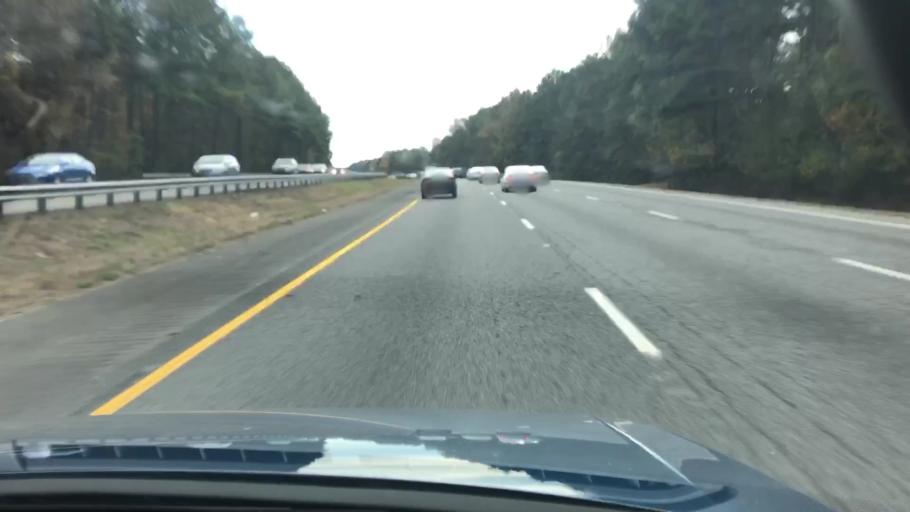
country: US
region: Georgia
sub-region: Henry County
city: Locust Grove
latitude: 33.2305
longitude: -84.0795
